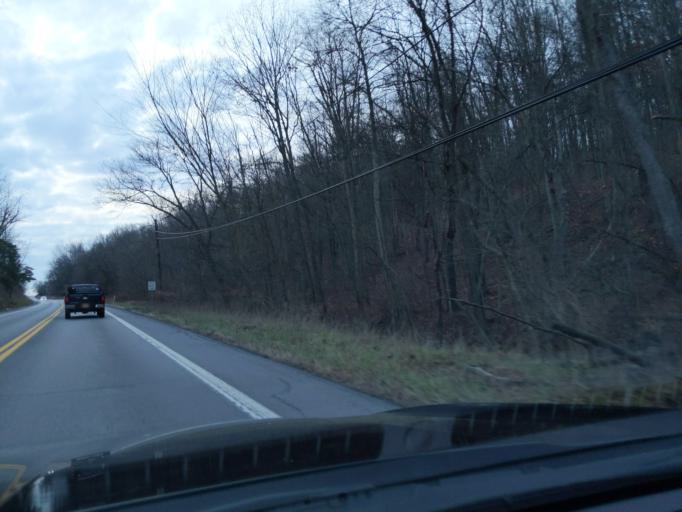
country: US
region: Pennsylvania
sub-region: Blair County
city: Lakemont
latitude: 40.4670
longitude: -78.3029
